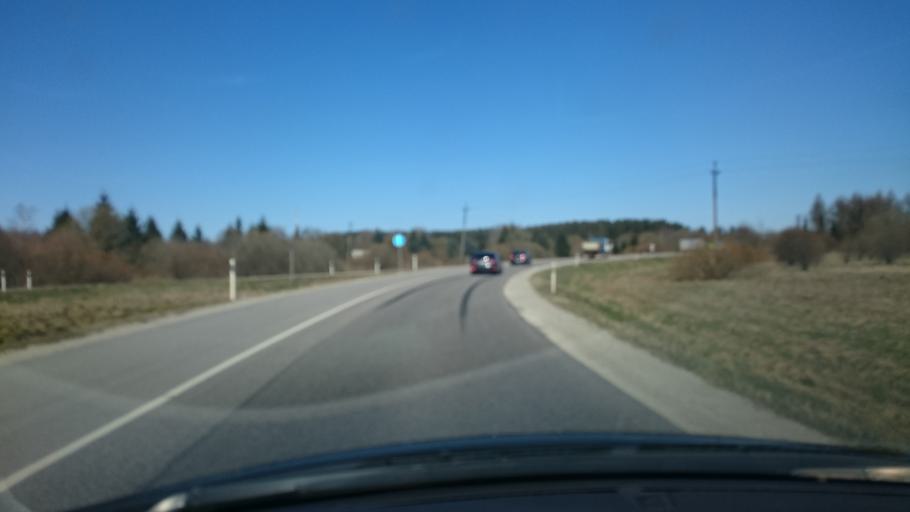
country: EE
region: Harju
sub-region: Tallinna linn
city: Kose
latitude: 59.4411
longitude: 24.9102
